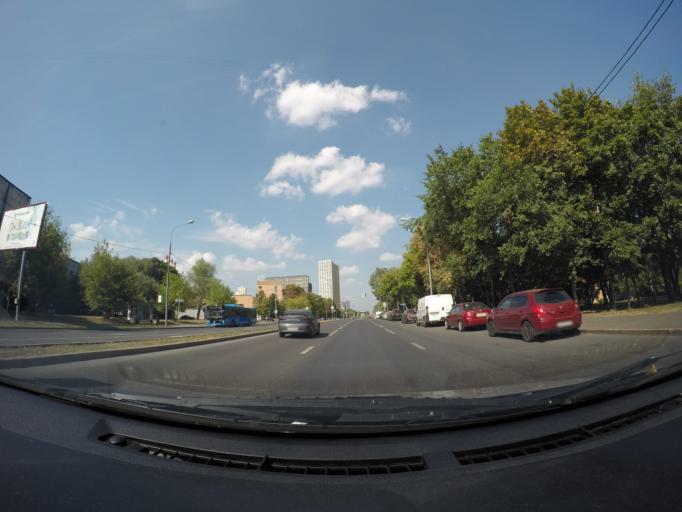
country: RU
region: Moskovskaya
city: Levoberezhnyy
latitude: 55.8627
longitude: 37.4861
